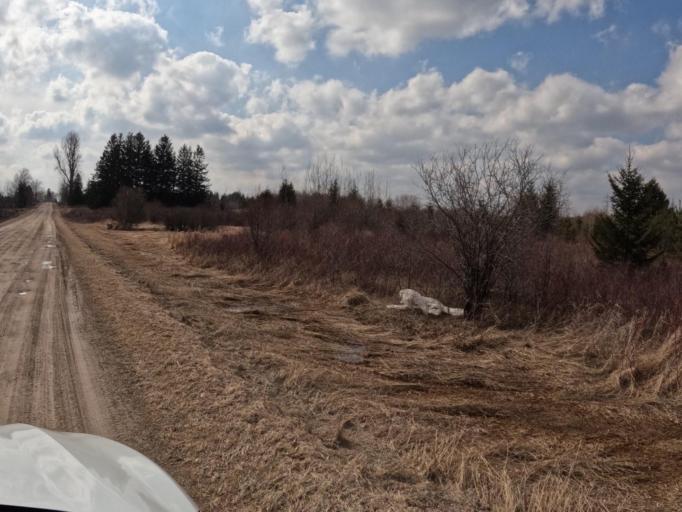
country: CA
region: Ontario
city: Shelburne
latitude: 43.9607
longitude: -80.3105
